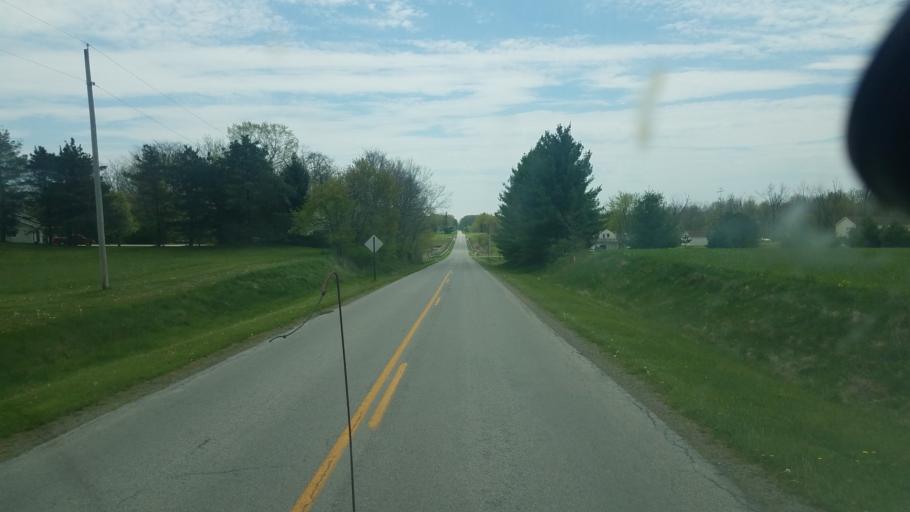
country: US
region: Ohio
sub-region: Allen County
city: Bluffton
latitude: 40.7827
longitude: -83.9692
